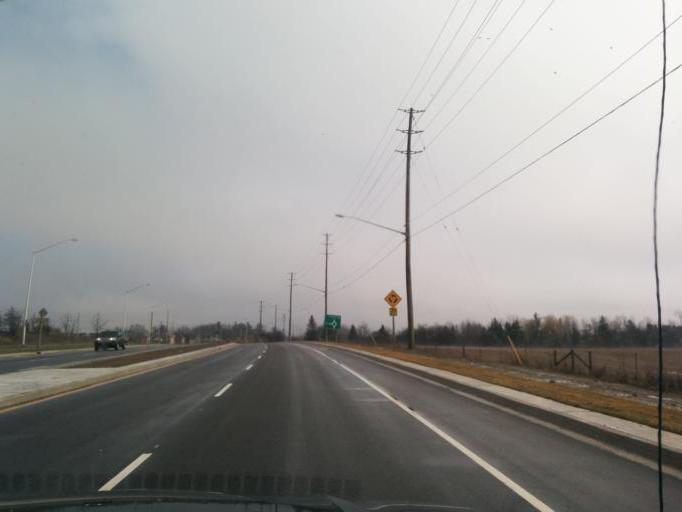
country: CA
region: Ontario
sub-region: Halton
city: Milton
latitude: 43.4970
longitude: -79.9002
